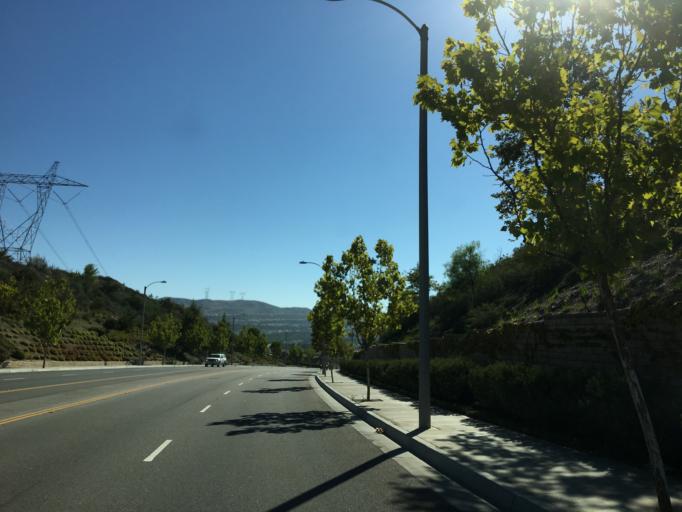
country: US
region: California
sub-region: Los Angeles County
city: Santa Clarita
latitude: 34.4425
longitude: -118.4926
